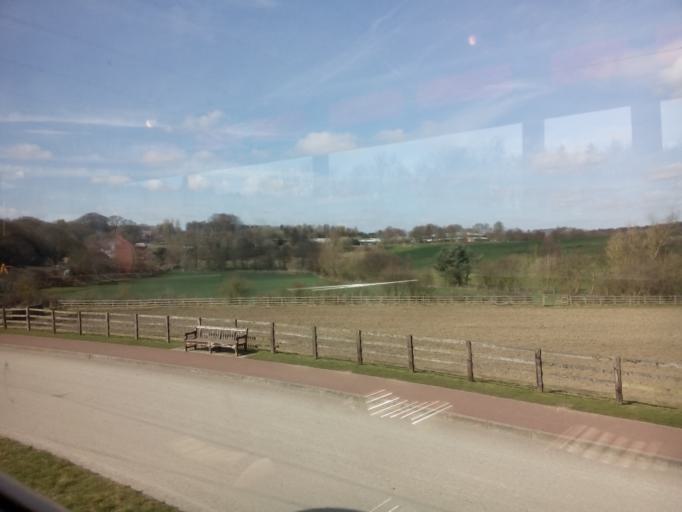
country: GB
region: England
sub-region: County Durham
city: Stanley
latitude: 54.8849
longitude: -1.6571
